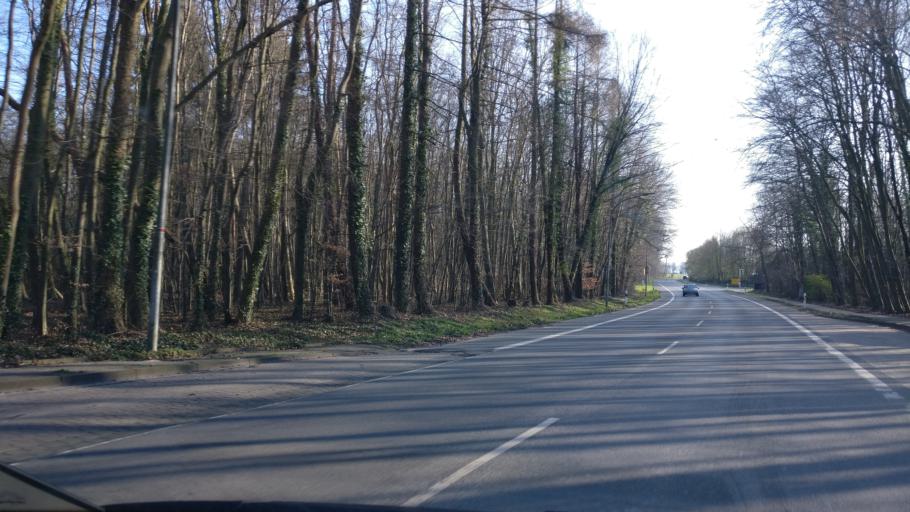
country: DE
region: North Rhine-Westphalia
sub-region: Regierungsbezirk Detmold
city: Lage
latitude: 52.0163
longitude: 8.7499
